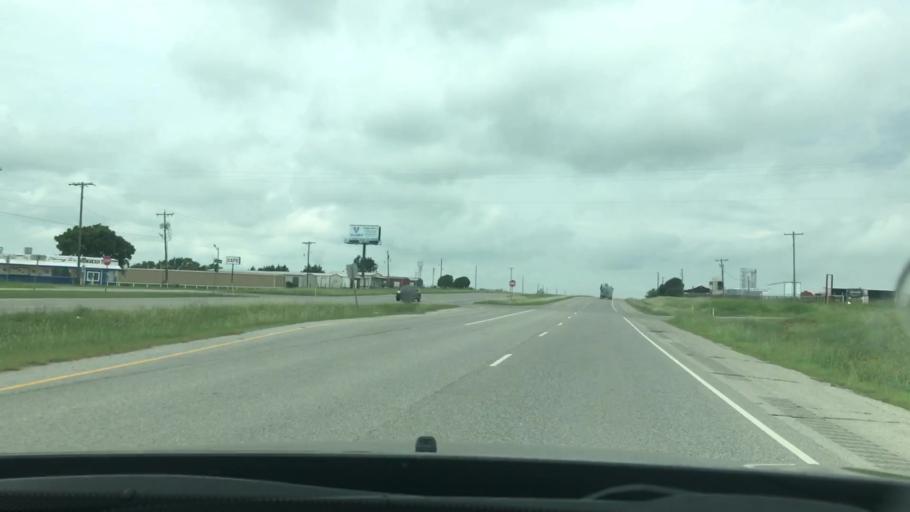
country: US
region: Oklahoma
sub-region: Carter County
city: Wilson
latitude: 34.1733
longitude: -97.4386
